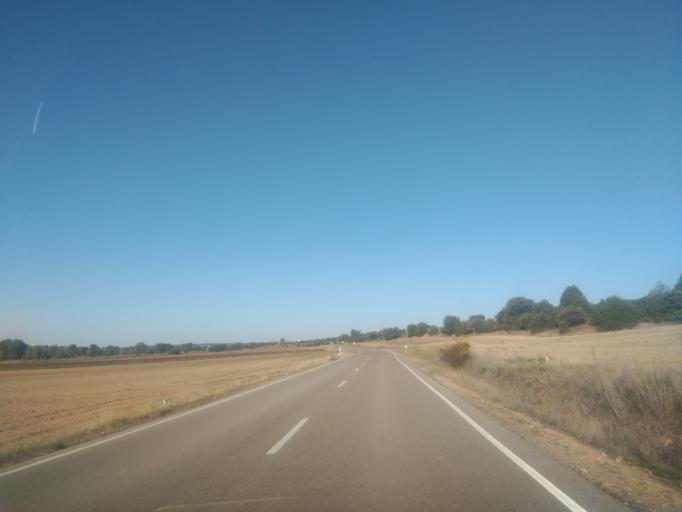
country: ES
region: Castille and Leon
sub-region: Provincia de Soria
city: Alcubilla de Avellaneda
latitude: 41.7227
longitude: -3.3192
